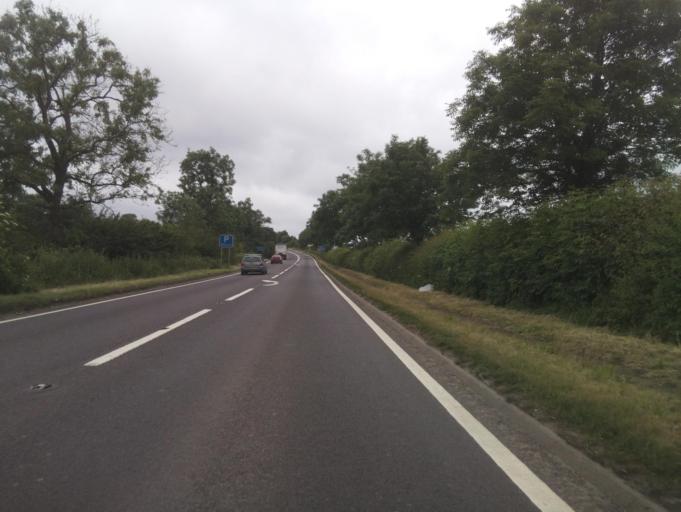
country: GB
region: England
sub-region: Leicestershire
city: Houghton on the Hill
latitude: 52.6251
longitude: -0.9774
